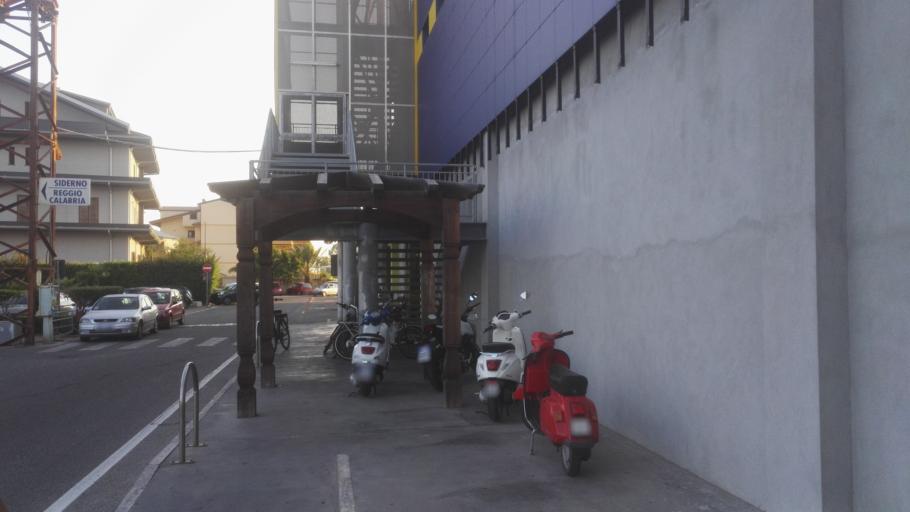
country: IT
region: Calabria
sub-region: Provincia di Reggio Calabria
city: Marina di Gioiosa Ionica
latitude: 38.2878
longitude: 16.3152
